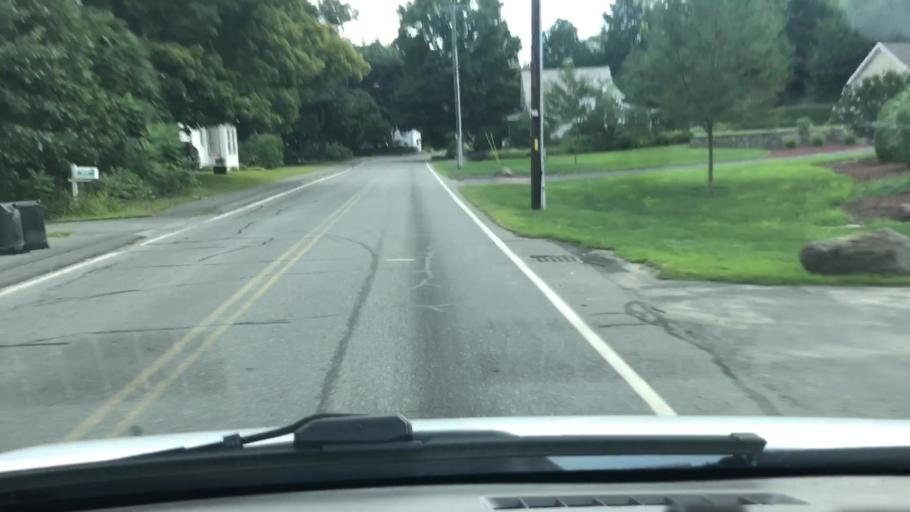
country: US
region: Massachusetts
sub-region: Franklin County
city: Turners Falls
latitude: 42.5886
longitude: -72.5689
